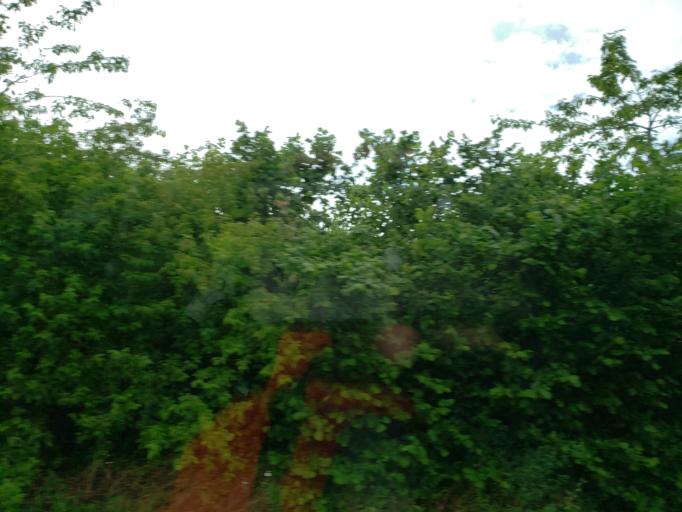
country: FR
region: Bourgogne
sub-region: Departement de l'Yonne
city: Venoy
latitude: 47.8049
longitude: 3.6675
